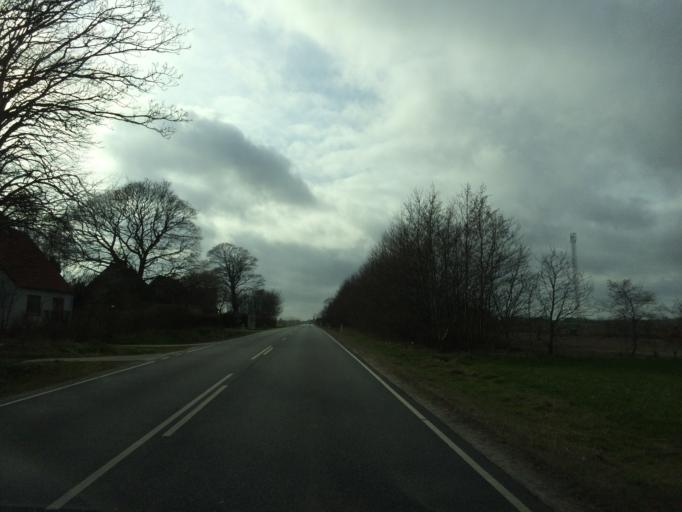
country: DK
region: Central Jutland
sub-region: Favrskov Kommune
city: Ulstrup
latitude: 56.4959
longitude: 9.8150
